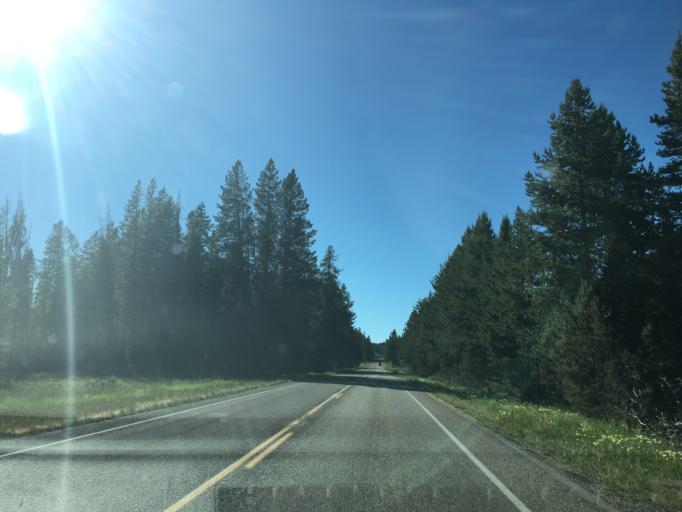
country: US
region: Wyoming
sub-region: Teton County
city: Jackson
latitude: 43.8583
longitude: -110.5282
